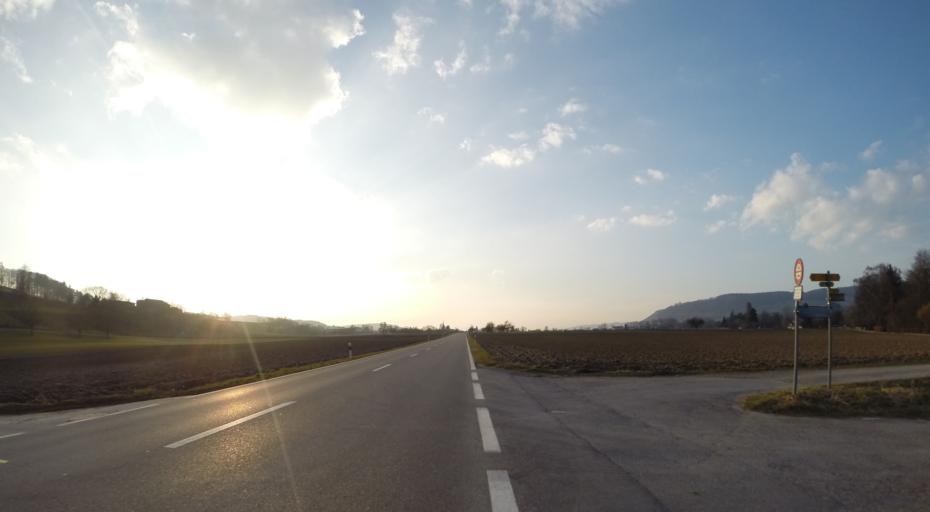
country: CH
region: Thurgau
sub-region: Frauenfeld District
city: Eschenz
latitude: 47.6440
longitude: 8.8895
